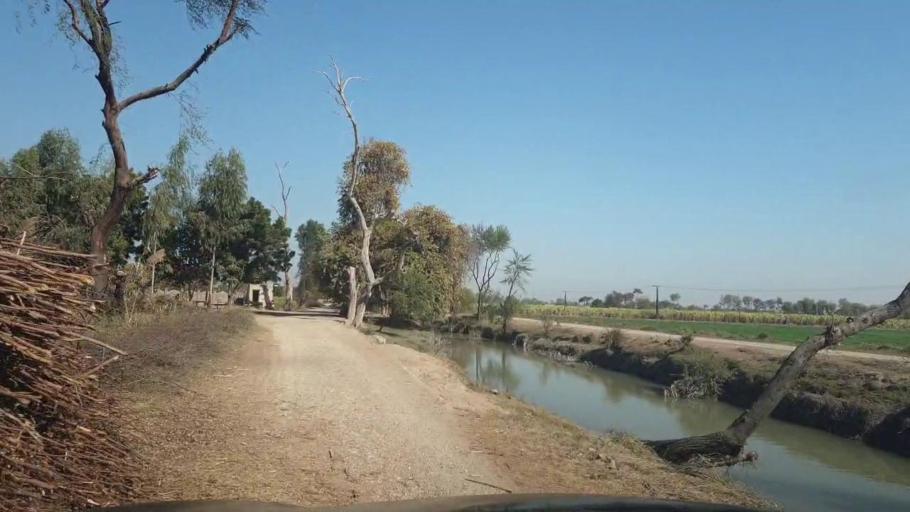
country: PK
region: Sindh
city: Ghotki
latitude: 27.9779
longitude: 69.4199
